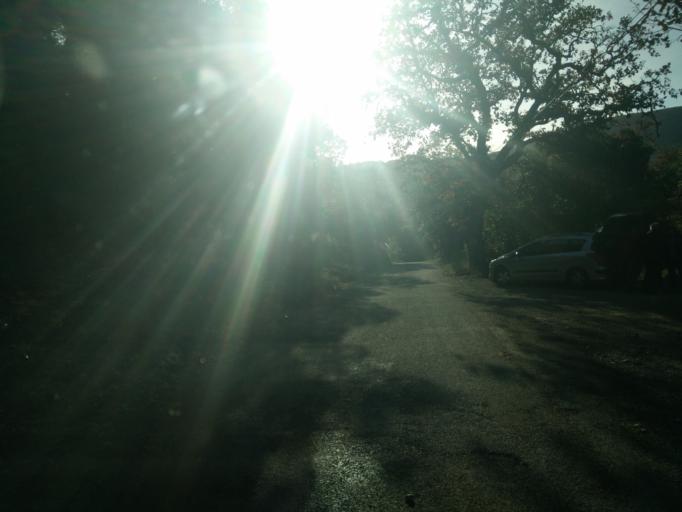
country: FR
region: Provence-Alpes-Cote d'Azur
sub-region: Departement du Var
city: Belgentier
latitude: 43.2134
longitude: 5.9735
